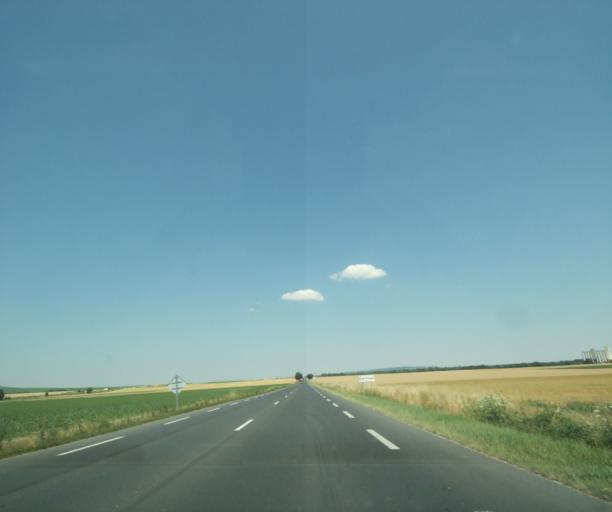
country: FR
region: Champagne-Ardenne
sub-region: Departement de la Marne
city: Verzy
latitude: 49.1495
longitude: 4.2134
